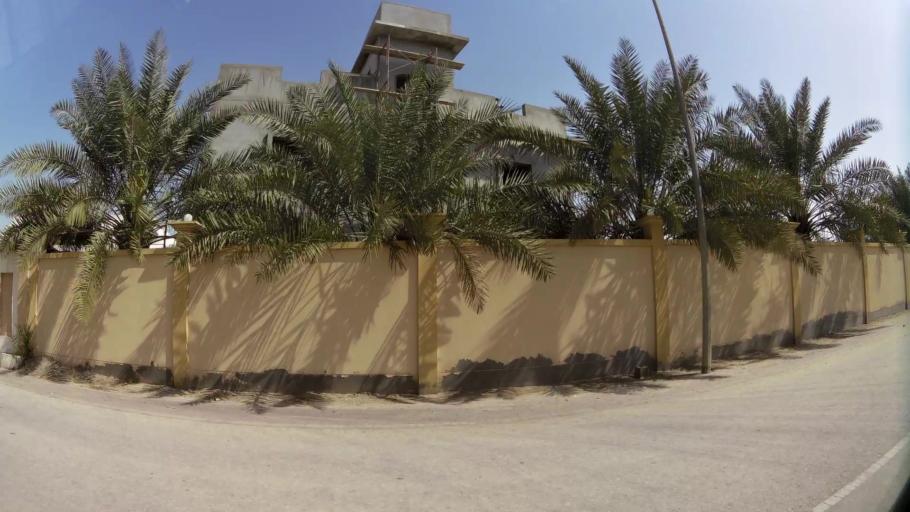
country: BH
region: Northern
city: Madinat `Isa
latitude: 26.1915
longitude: 50.4602
